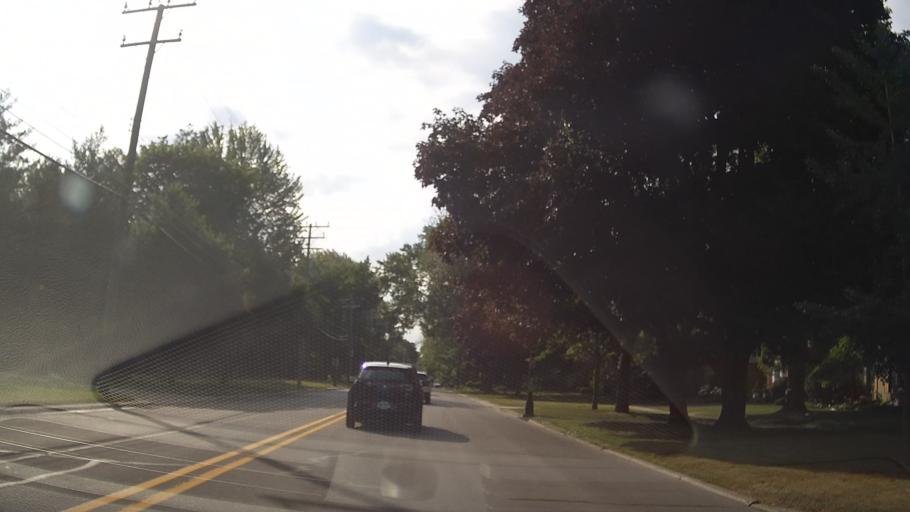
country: US
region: Michigan
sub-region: Wayne County
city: Grosse Pointe Farms
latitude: 42.4146
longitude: -82.9048
